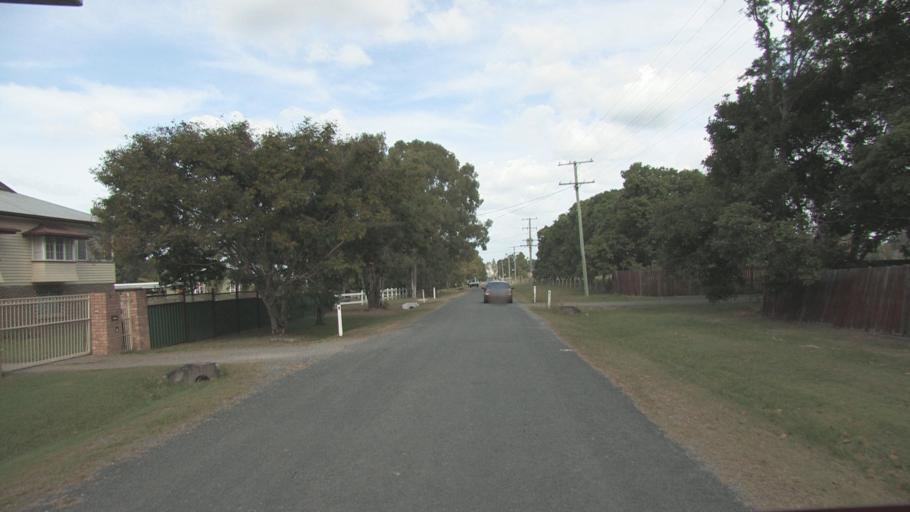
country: AU
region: Queensland
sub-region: Logan
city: Waterford West
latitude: -27.6777
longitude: 153.1593
